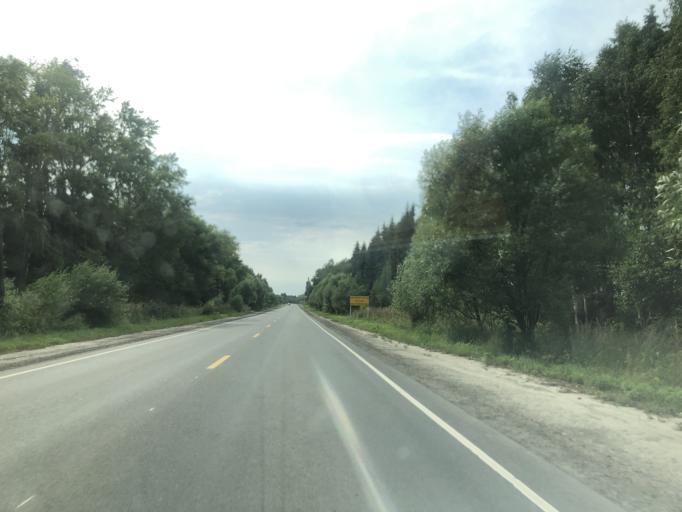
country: RU
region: Ivanovo
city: Shuya
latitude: 56.8533
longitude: 41.5639
